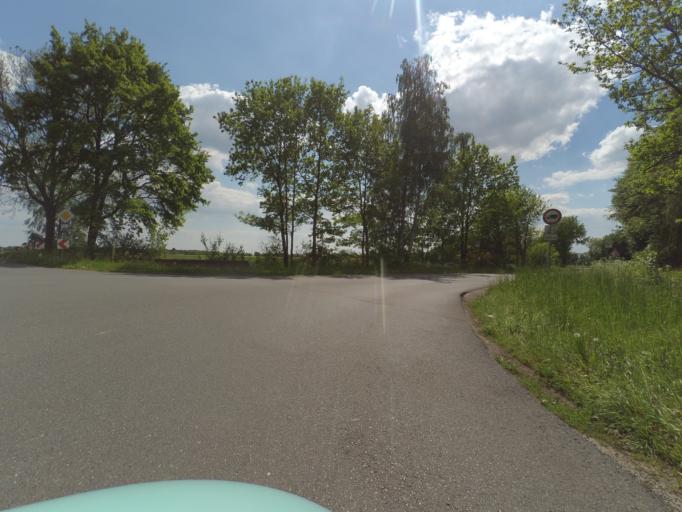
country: DE
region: Lower Saxony
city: Muden
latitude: 52.5124
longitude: 10.3694
